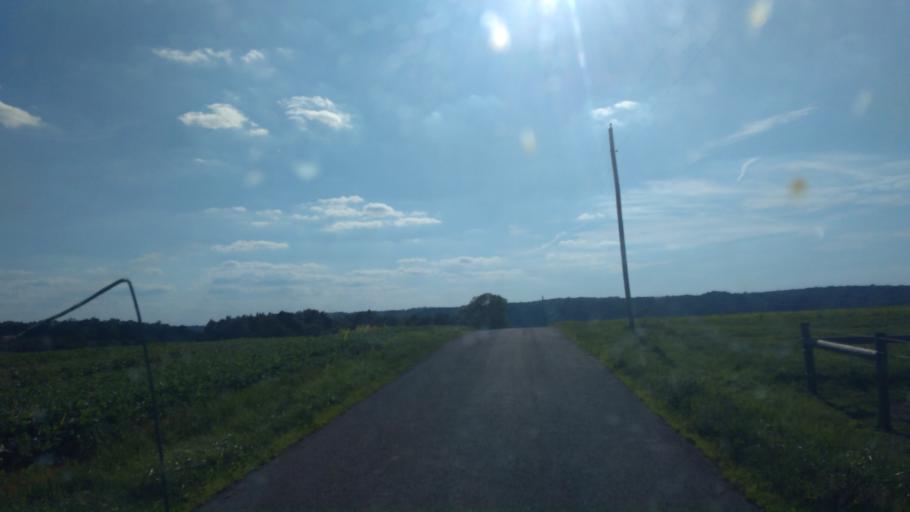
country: US
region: Ohio
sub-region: Wayne County
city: Shreve
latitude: 40.7338
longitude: -82.1303
